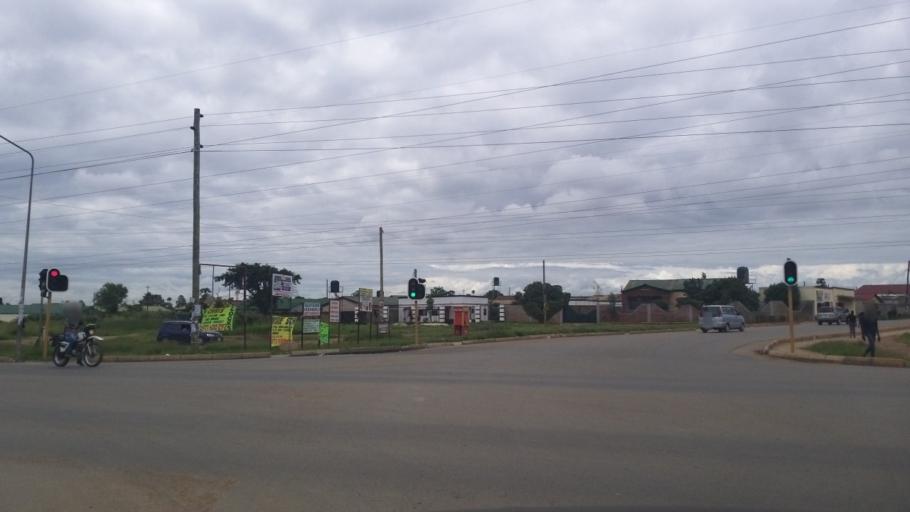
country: ZM
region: Lusaka
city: Lusaka
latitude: -15.4458
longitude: 28.3052
